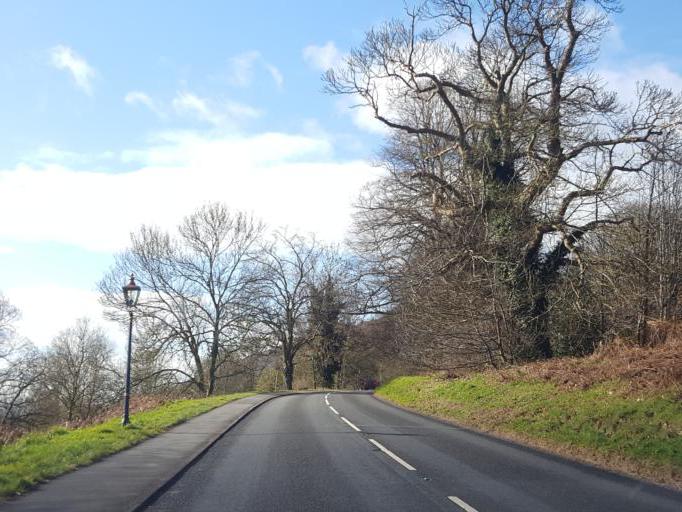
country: GB
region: England
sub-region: Worcestershire
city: Great Malvern
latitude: 52.1001
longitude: -2.3303
